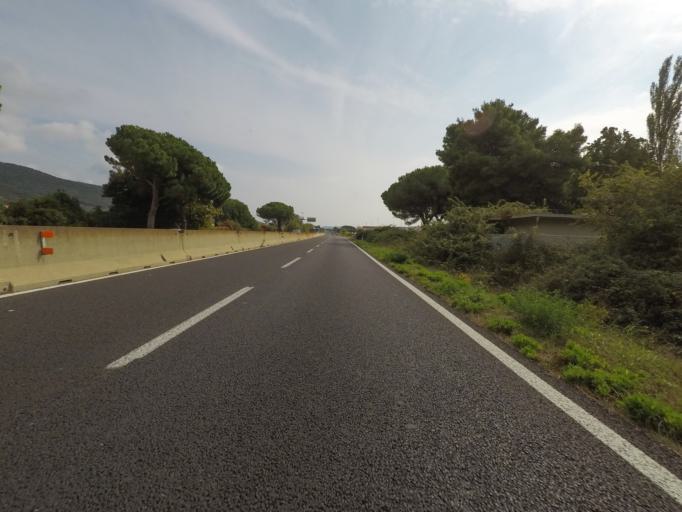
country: IT
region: Tuscany
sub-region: Provincia di Grosseto
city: Orbetello Scalo
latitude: 42.4691
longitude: 11.2379
